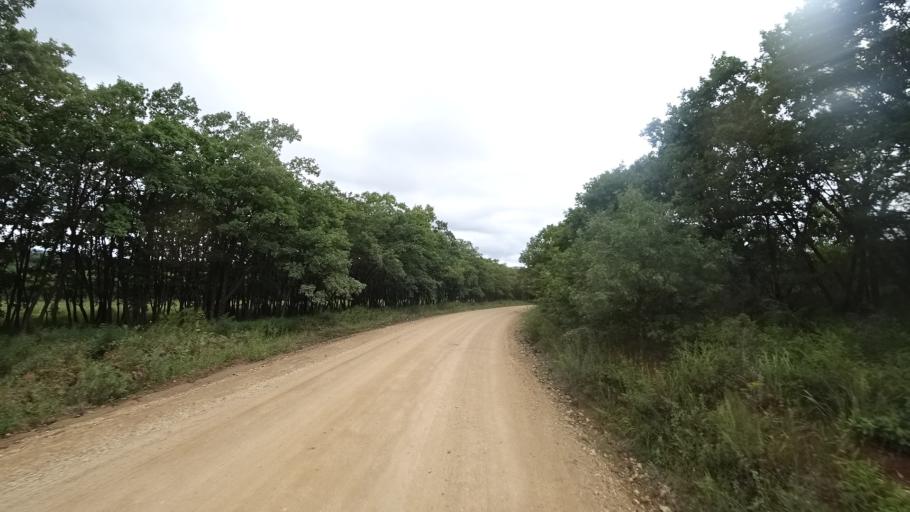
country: RU
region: Primorskiy
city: Chernigovka
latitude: 44.3398
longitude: 132.6217
